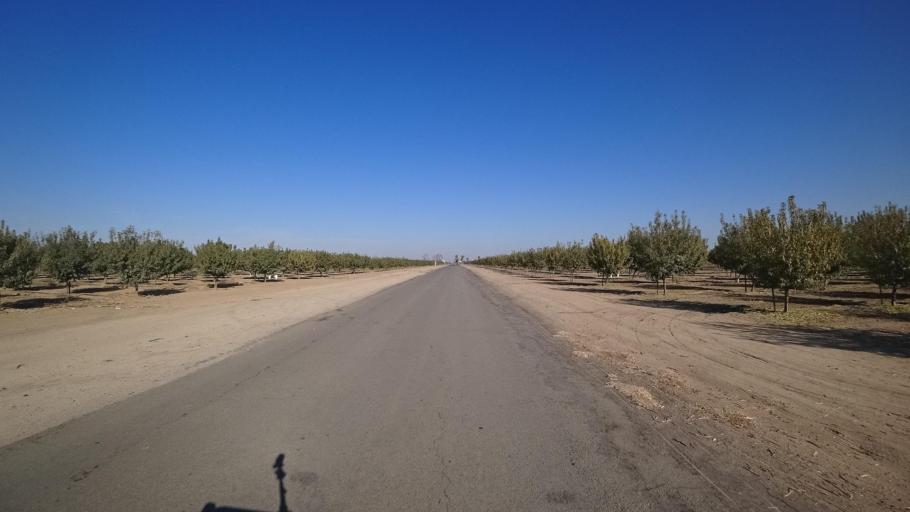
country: US
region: California
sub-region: Kern County
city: Delano
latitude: 35.7556
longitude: -119.2319
